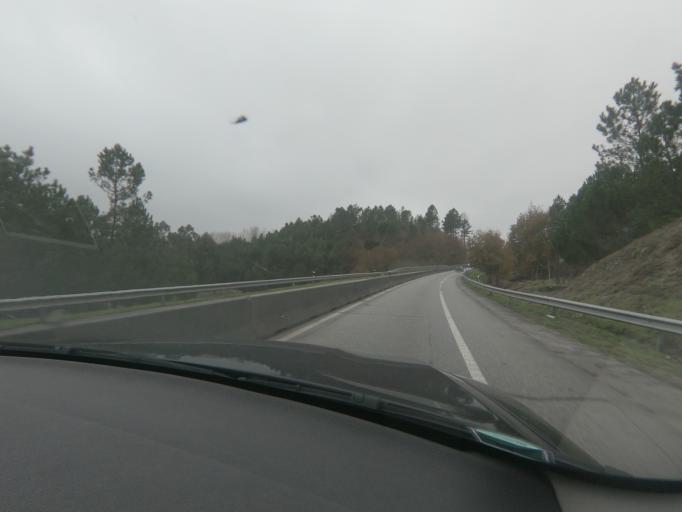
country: PT
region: Viseu
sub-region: Viseu
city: Viseu
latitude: 40.6015
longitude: -7.9850
